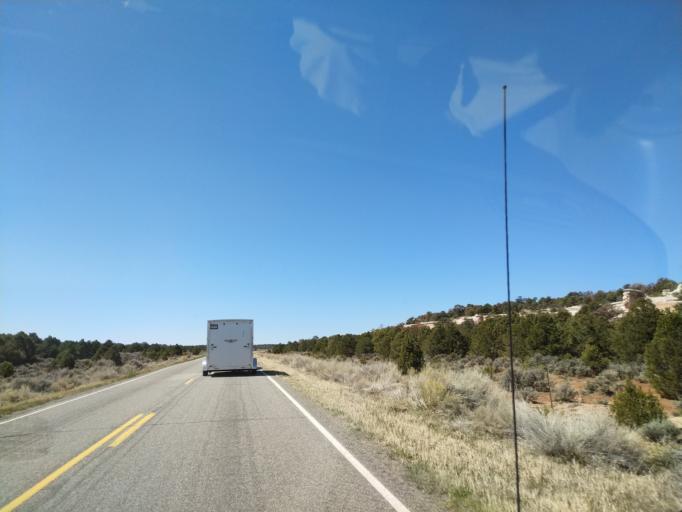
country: US
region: Colorado
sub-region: Mesa County
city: Redlands
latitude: 39.0074
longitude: -108.6855
